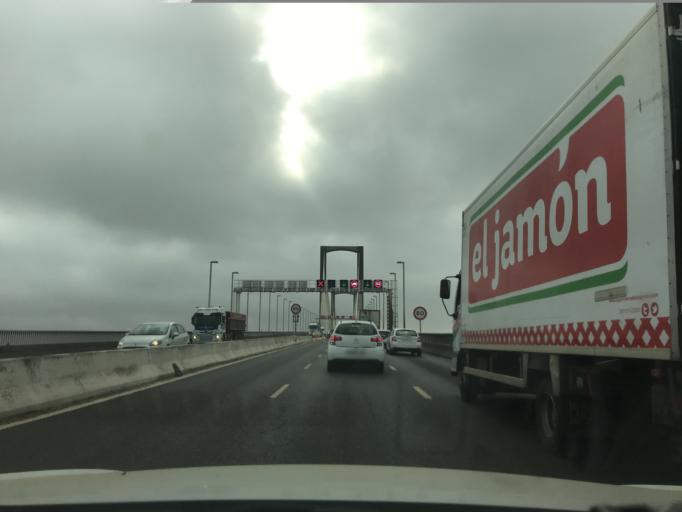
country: ES
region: Andalusia
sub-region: Provincia de Sevilla
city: Gelves
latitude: 37.3527
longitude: -5.9973
